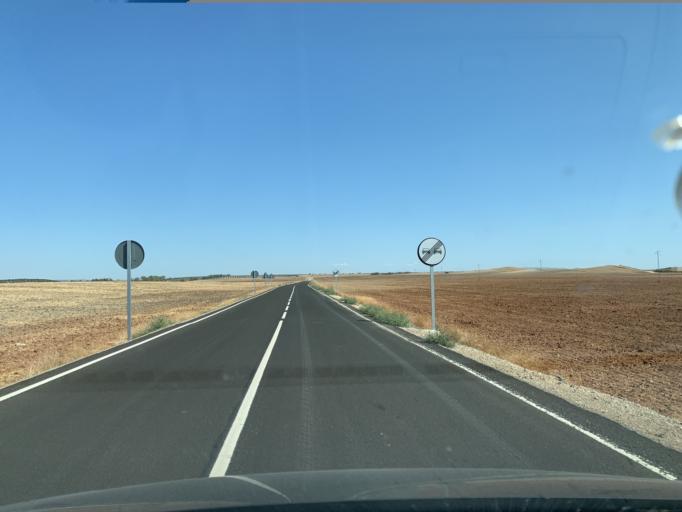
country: ES
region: Andalusia
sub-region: Provincia de Sevilla
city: Marchena
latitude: 37.3252
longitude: -5.3428
